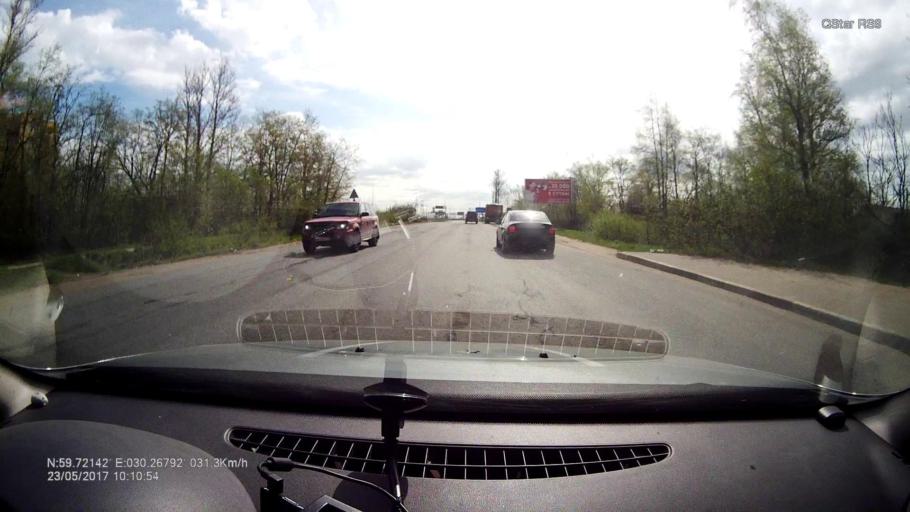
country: RU
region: St.-Petersburg
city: Aleksandrovskaya
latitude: 59.7214
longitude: 30.2681
